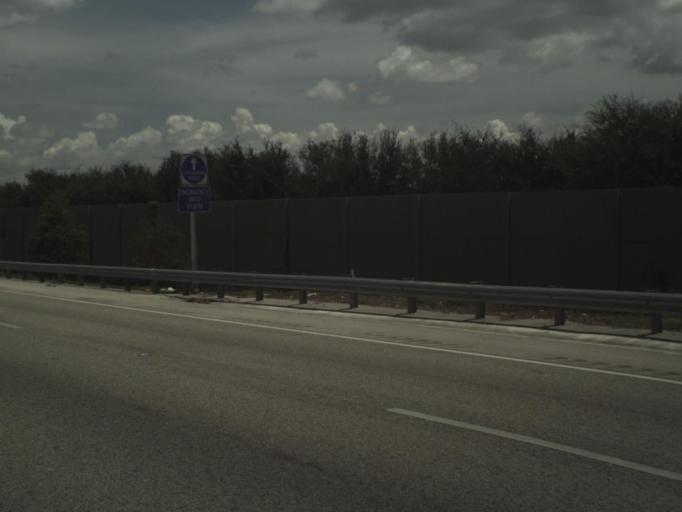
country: US
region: Florida
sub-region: Miami-Dade County
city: Palm Springs North
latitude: 25.9597
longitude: -80.3515
